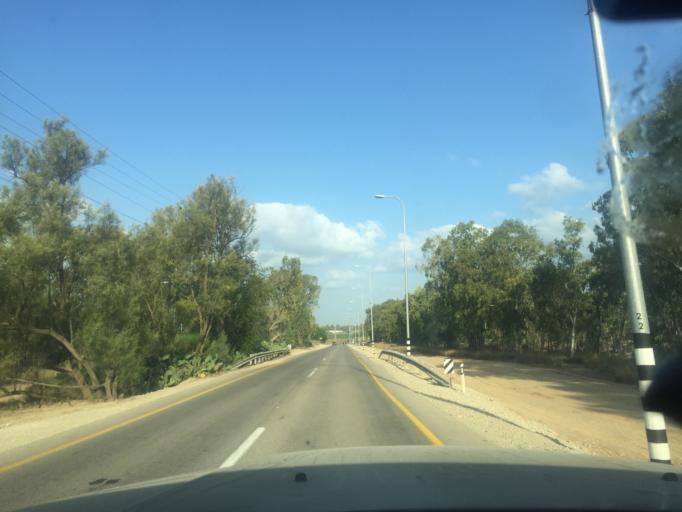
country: PS
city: Umm an Nasr
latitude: 31.6045
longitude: 34.5630
